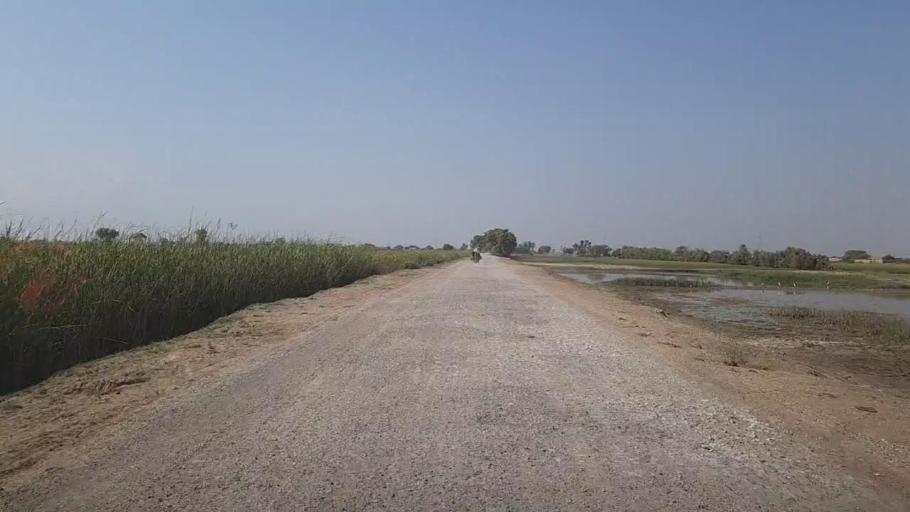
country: PK
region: Sindh
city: Kandhkot
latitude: 28.4020
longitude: 69.2611
